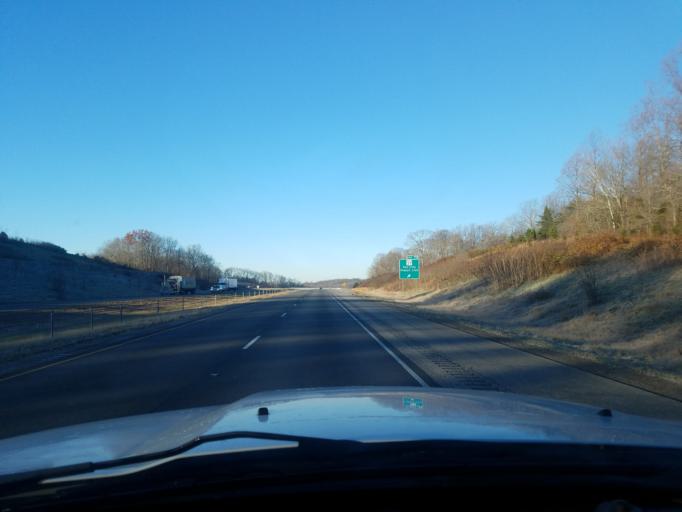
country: US
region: Indiana
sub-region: Crawford County
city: English
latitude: 38.2280
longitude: -86.5831
